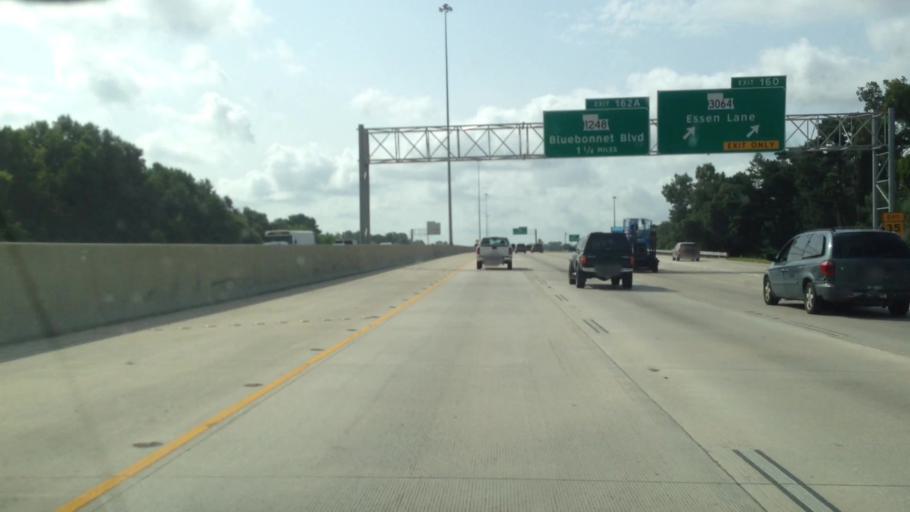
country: US
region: Louisiana
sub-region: East Baton Rouge Parish
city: Westminster
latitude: 30.4112
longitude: -91.1061
